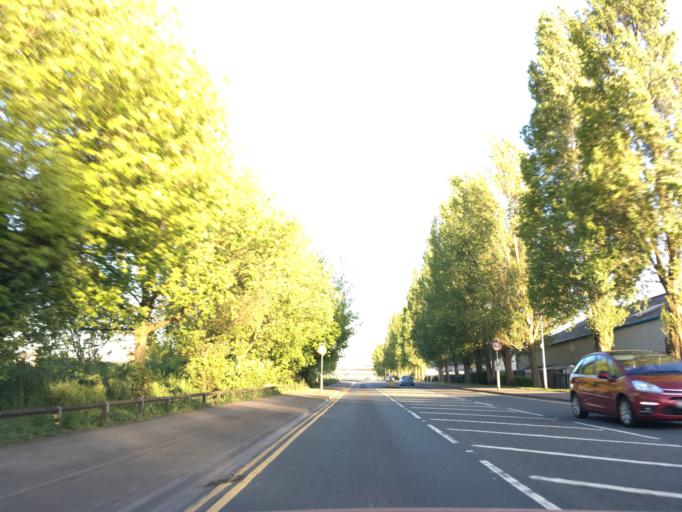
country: GB
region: Wales
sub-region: Newport
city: Newport
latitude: 51.5787
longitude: -2.9836
